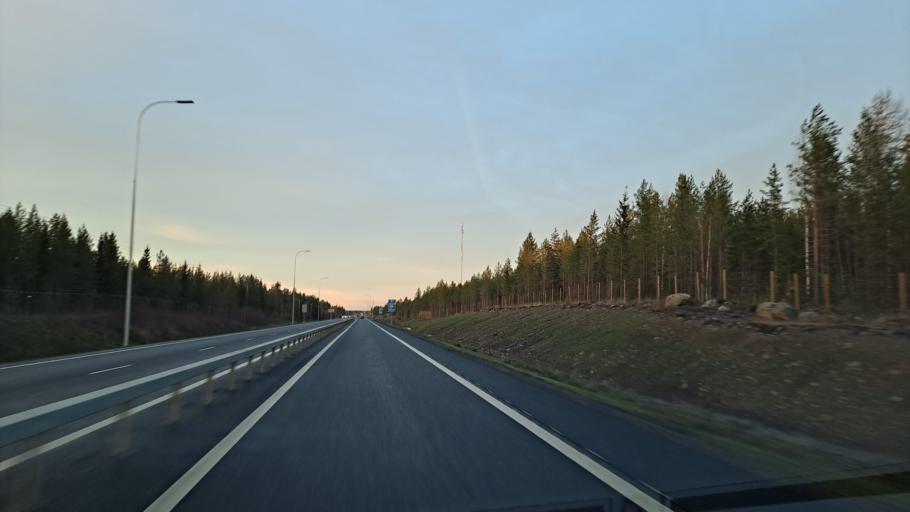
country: FI
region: Northern Ostrobothnia
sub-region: Oulu
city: Haukipudas
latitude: 65.2285
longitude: 25.3930
